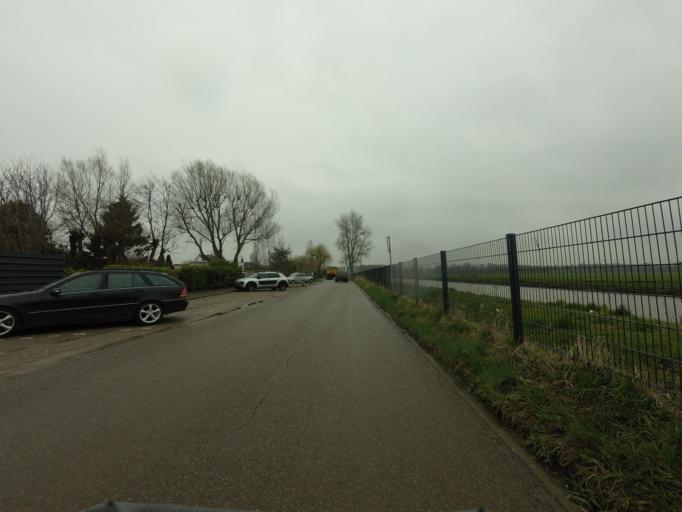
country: NL
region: Utrecht
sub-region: Stichtse Vecht
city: Breukelen
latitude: 52.1821
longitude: 5.0193
